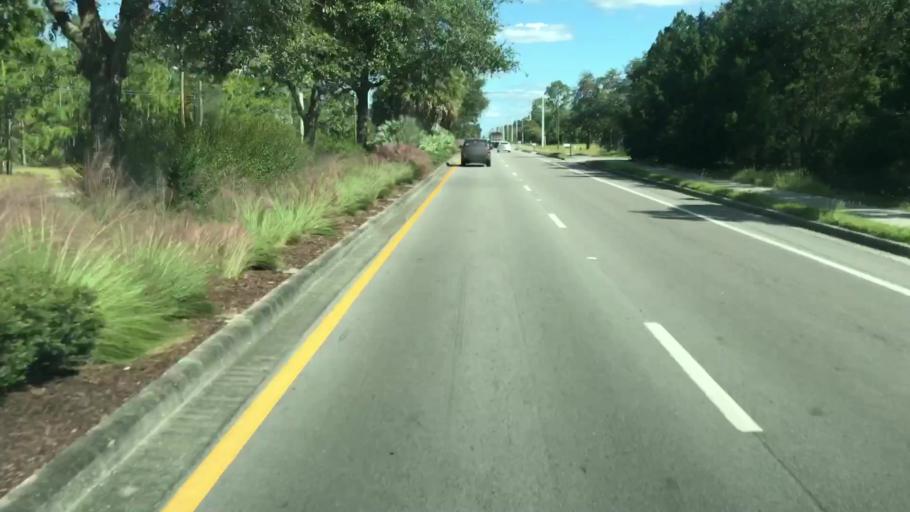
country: US
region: Florida
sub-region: Collier County
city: Vineyards
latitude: 26.2292
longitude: -81.6557
